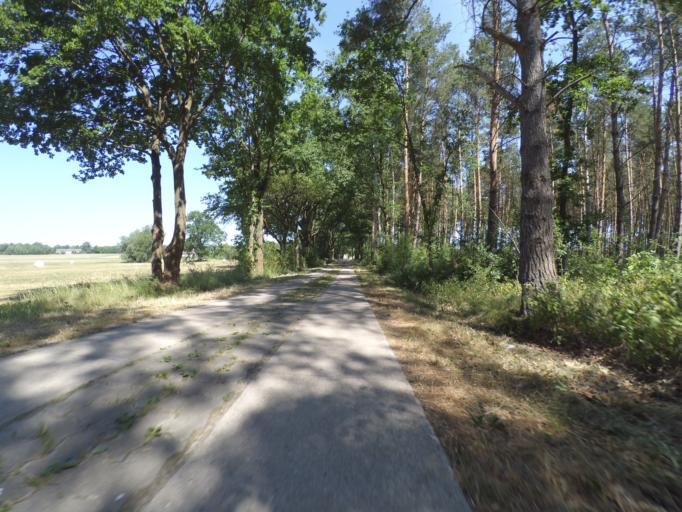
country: DE
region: Brandenburg
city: Heiligengrabe
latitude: 53.2172
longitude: 12.3290
